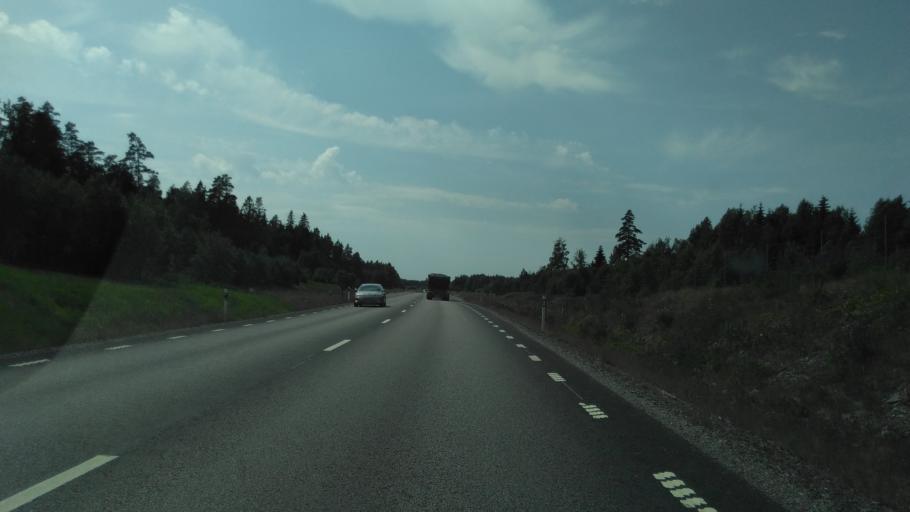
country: SE
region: Vaestra Goetaland
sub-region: Lidkopings Kommun
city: Lidkoping
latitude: 58.4569
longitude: 13.0009
